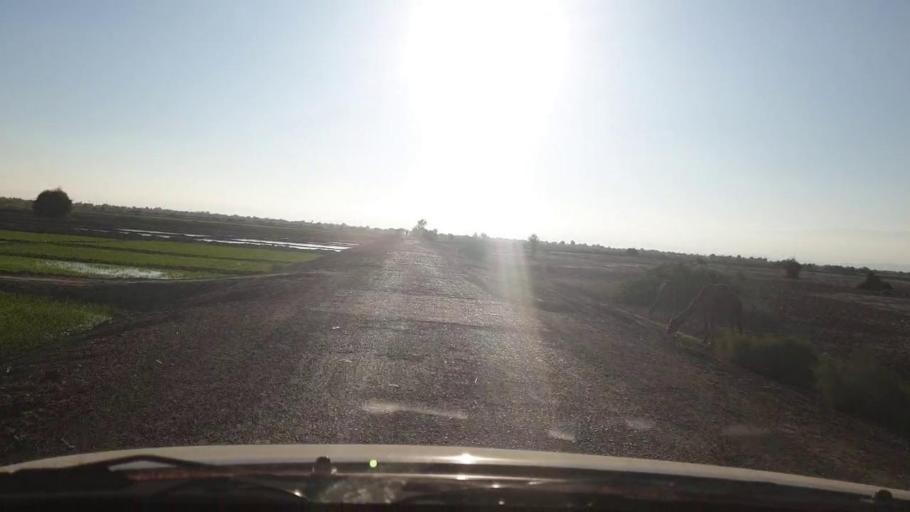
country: PK
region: Sindh
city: Johi
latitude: 26.7741
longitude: 67.4512
